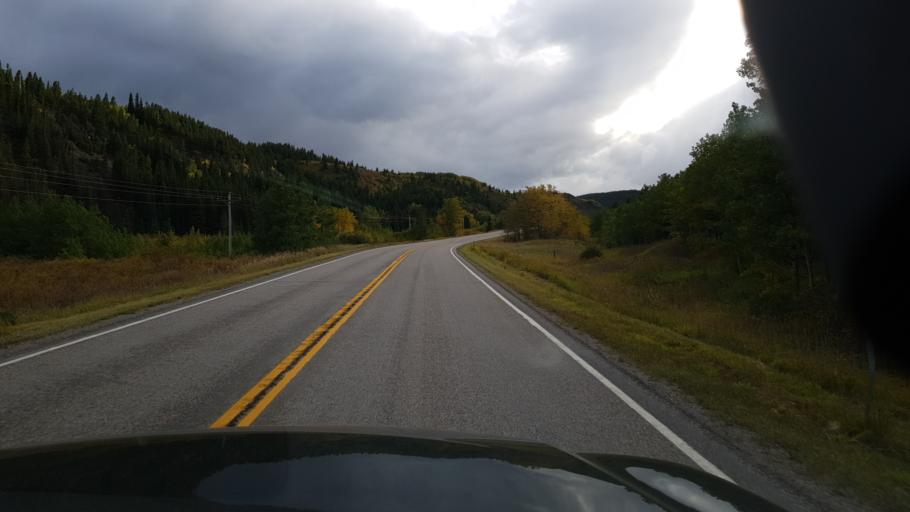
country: US
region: Montana
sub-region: Glacier County
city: South Browning
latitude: 48.3501
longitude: -113.3063
